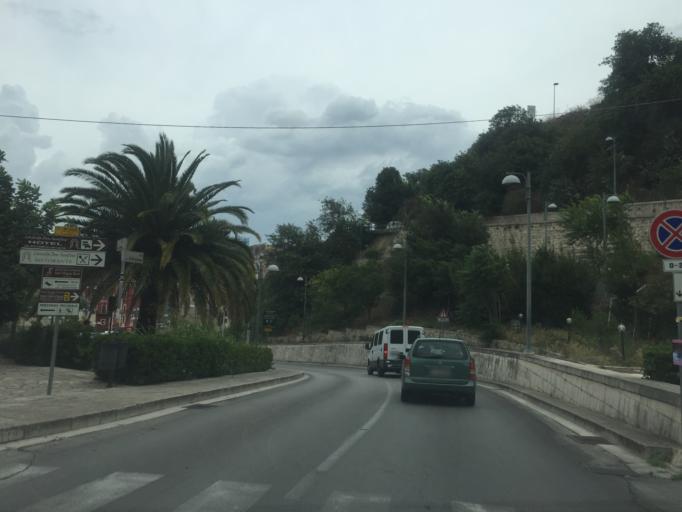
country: IT
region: Sicily
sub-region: Ragusa
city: Ragusa
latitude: 36.9242
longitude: 14.7362
